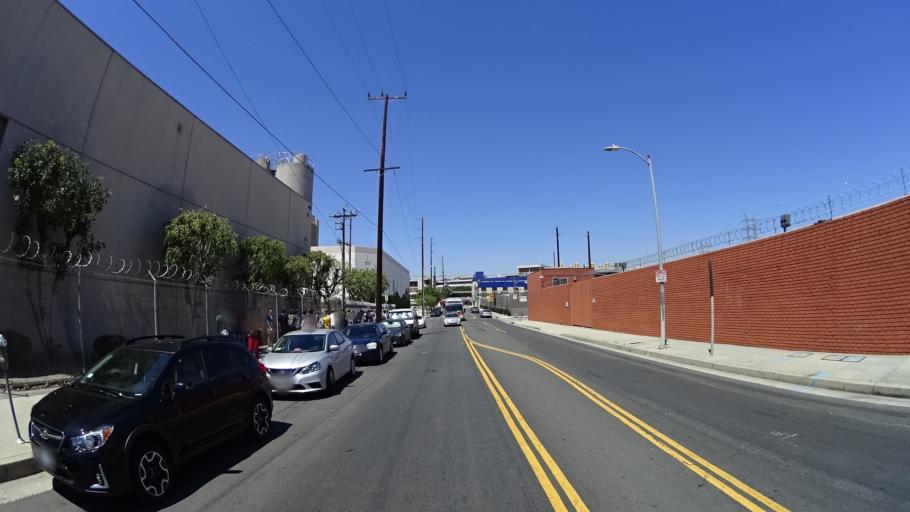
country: US
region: California
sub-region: Los Angeles County
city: Los Angeles
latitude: 34.0511
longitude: -118.2314
